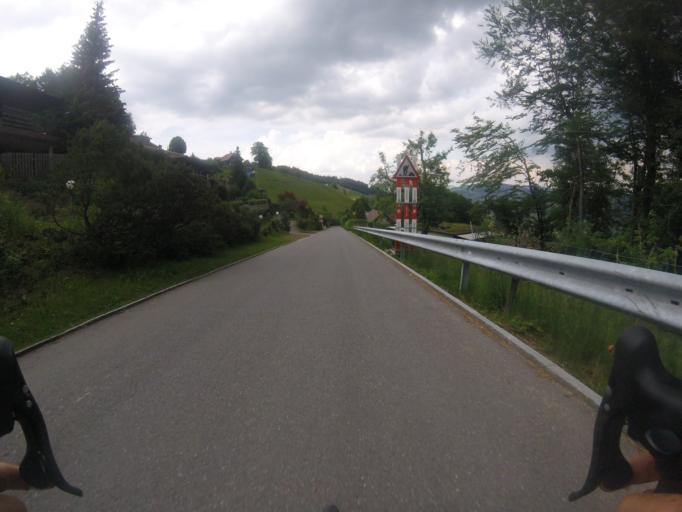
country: CH
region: Bern
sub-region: Bern-Mittelland District
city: Muhlethurnen
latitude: 46.8375
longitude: 7.5399
